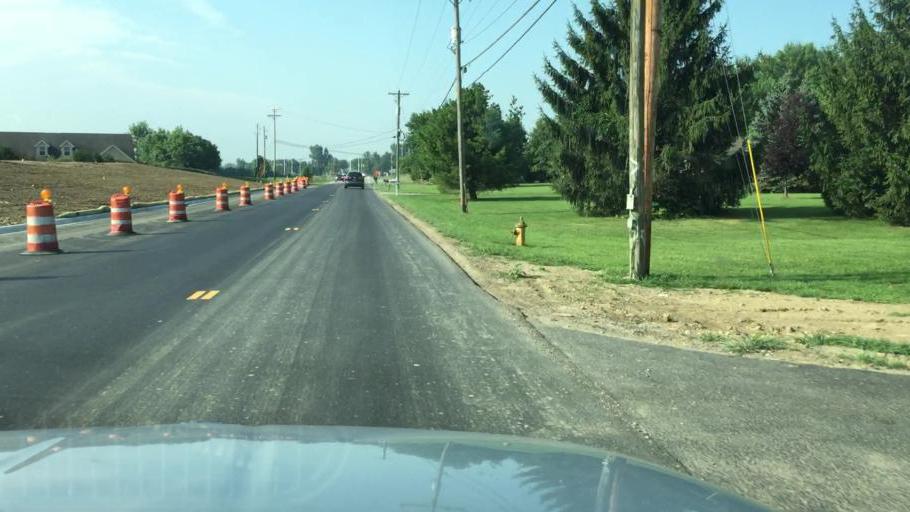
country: US
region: Ohio
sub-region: Franklin County
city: Hilliard
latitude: 40.0681
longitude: -83.1600
